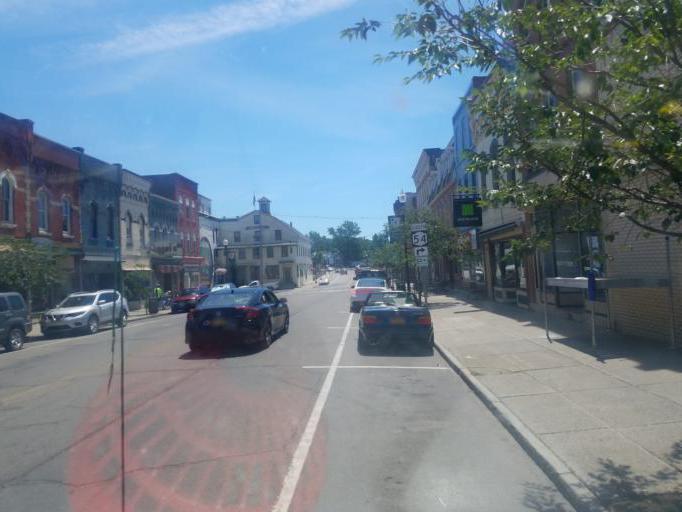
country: US
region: New York
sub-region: Yates County
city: Penn Yan
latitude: 42.6607
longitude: -77.0536
